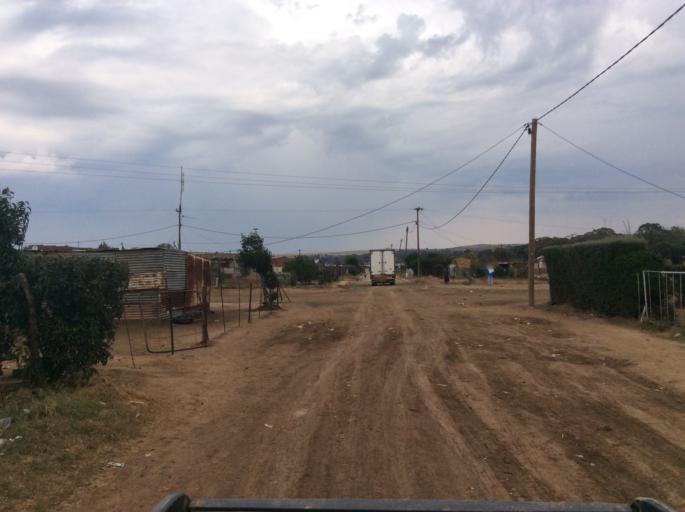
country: ZA
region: Orange Free State
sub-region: Xhariep District Municipality
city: Dewetsdorp
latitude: -29.5756
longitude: 26.6830
